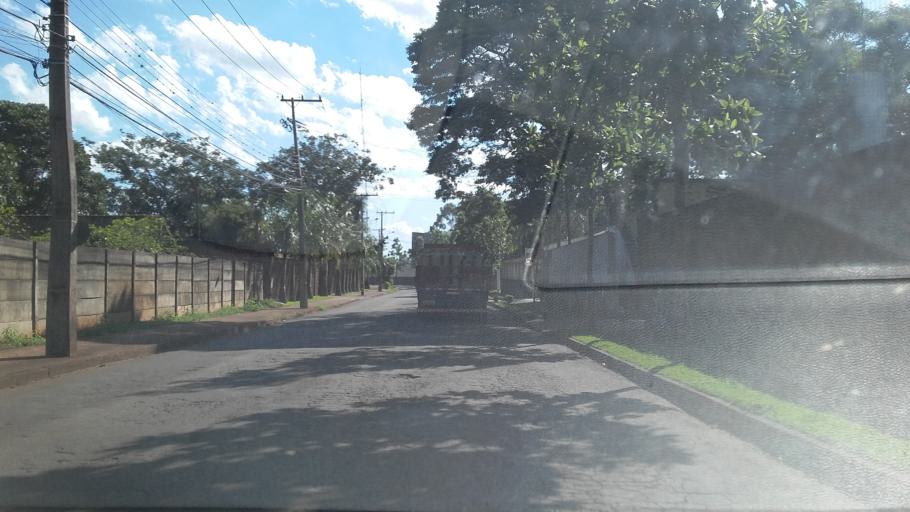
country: BR
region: Parana
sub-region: Londrina
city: Londrina
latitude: -23.2927
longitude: -51.2081
